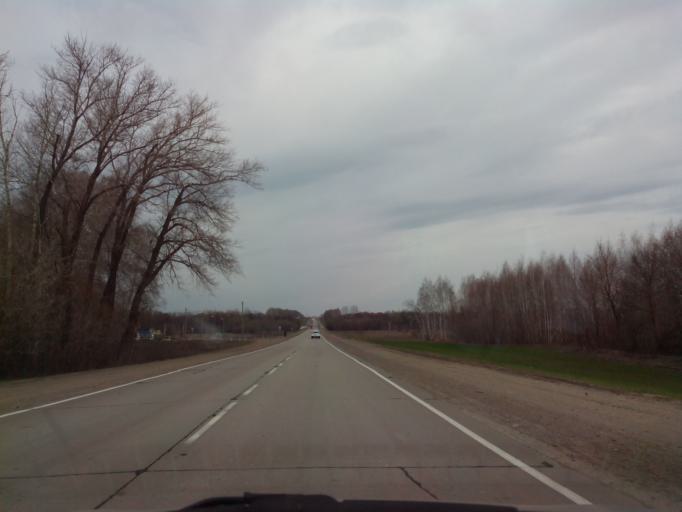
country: RU
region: Tambov
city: Znamenka
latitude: 52.3907
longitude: 41.4028
